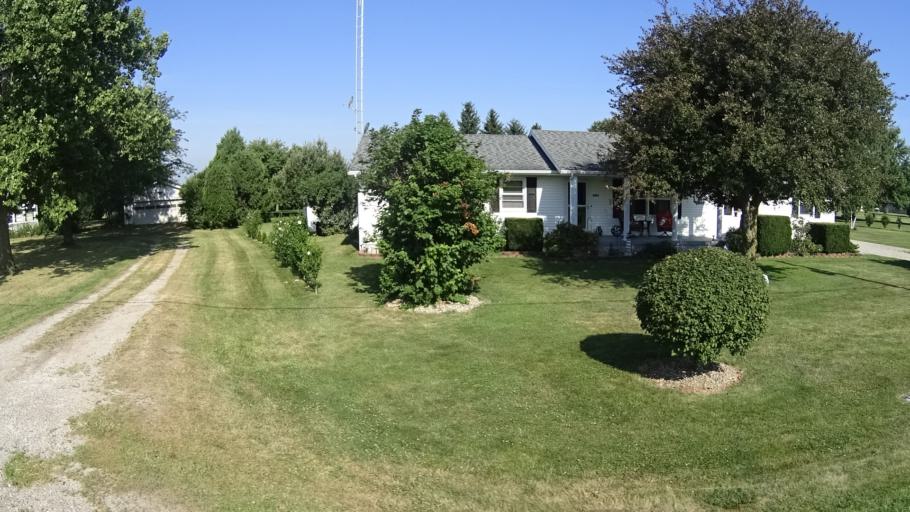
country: US
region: Ohio
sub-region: Huron County
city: Bellevue
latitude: 41.3855
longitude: -82.8361
